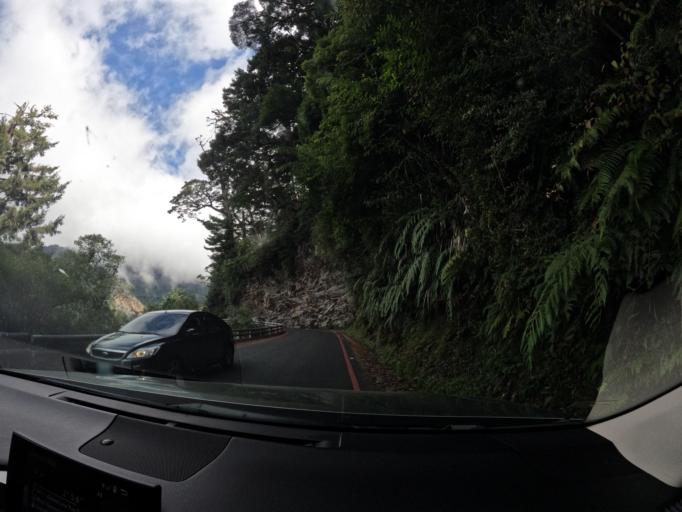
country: TW
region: Taiwan
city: Yujing
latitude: 23.2669
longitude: 120.9383
